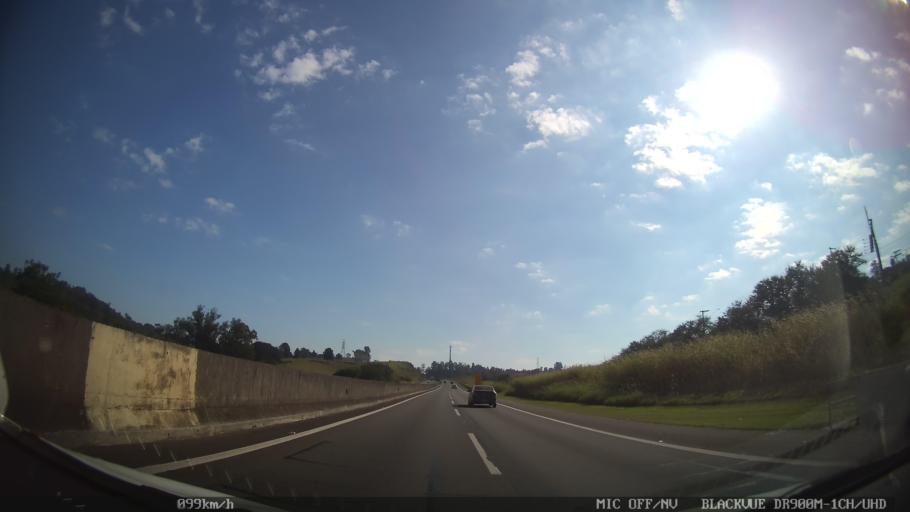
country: BR
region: Sao Paulo
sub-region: Vinhedo
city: Vinhedo
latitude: -23.0354
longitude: -47.0103
